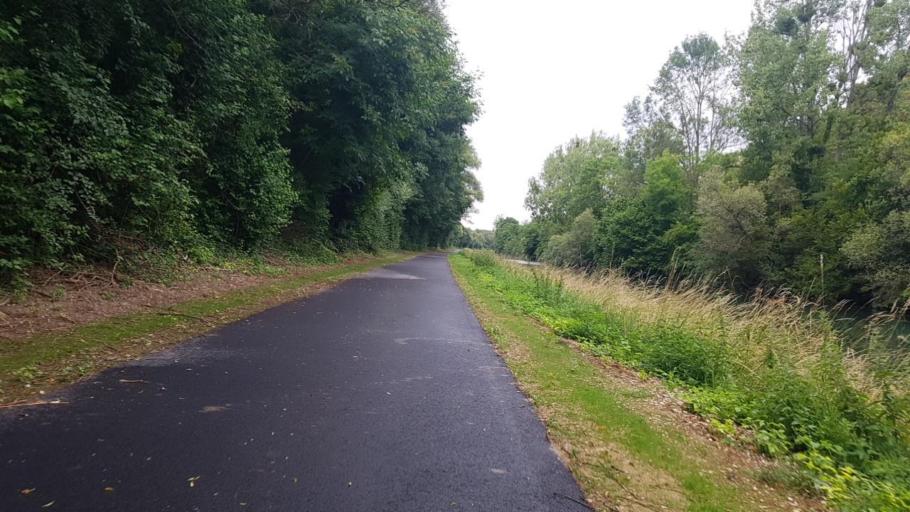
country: FR
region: Champagne-Ardenne
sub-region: Departement de la Marne
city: Vitry-le-Francois
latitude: 48.7729
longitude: 4.5486
